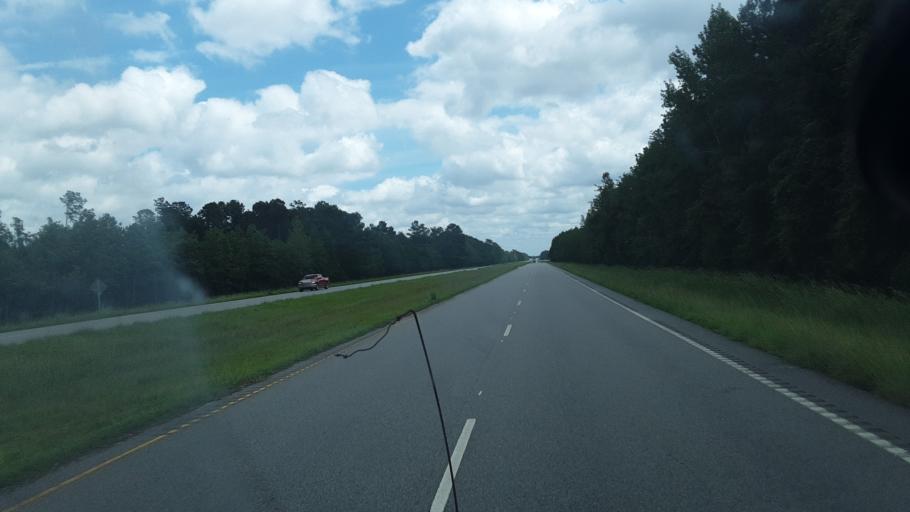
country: US
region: South Carolina
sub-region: Horry County
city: Loris
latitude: 34.0925
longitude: -78.9053
